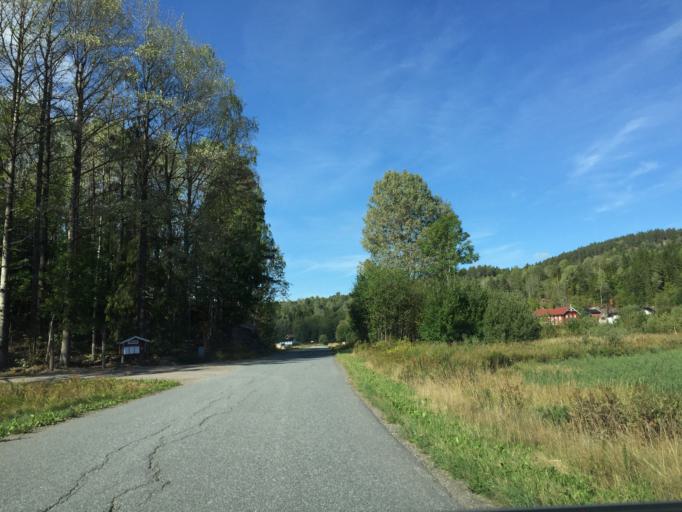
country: NO
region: Vestfold
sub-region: Holmestrand
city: Gullhaug
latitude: 59.4839
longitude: 10.1668
